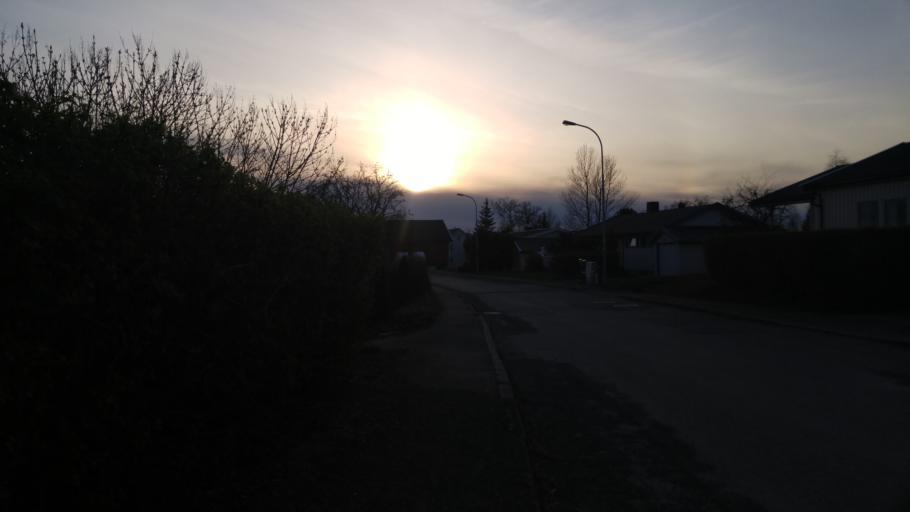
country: NO
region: Sor-Trondelag
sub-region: Trondheim
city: Trondheim
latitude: 63.4076
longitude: 10.4438
